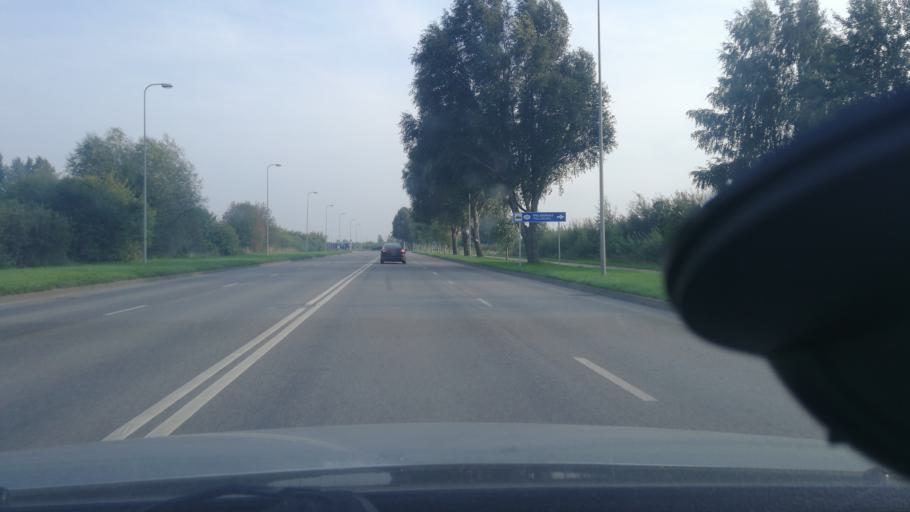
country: LT
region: Klaipedos apskritis
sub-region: Klaipeda
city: Klaipeda
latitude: 55.6574
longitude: 21.1700
